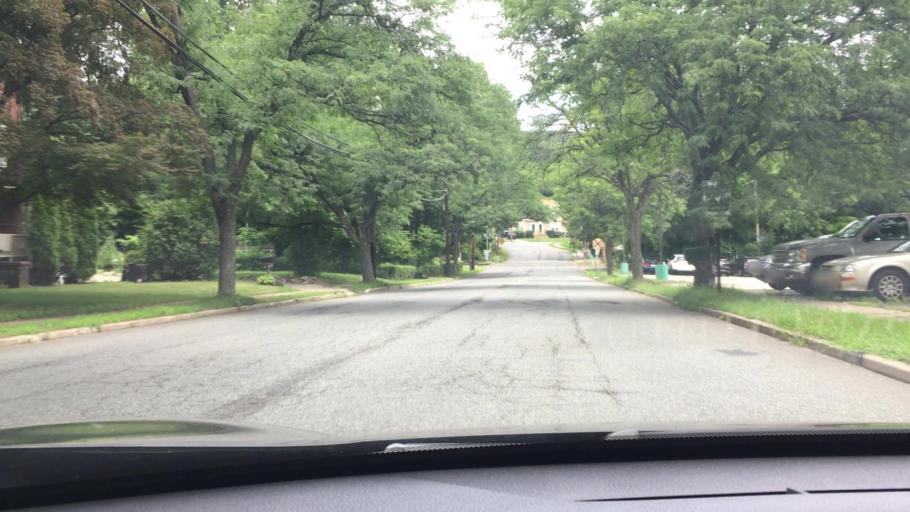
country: US
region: New Jersey
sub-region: Morris County
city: Boonton
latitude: 40.9119
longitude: -74.3918
